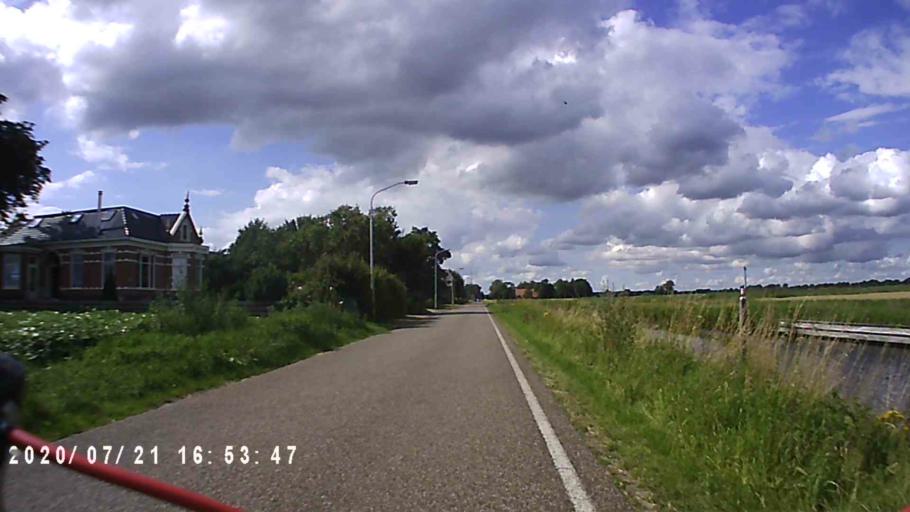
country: NL
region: Groningen
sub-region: Gemeente Hoogezand-Sappemeer
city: Hoogezand
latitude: 53.1265
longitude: 6.7689
